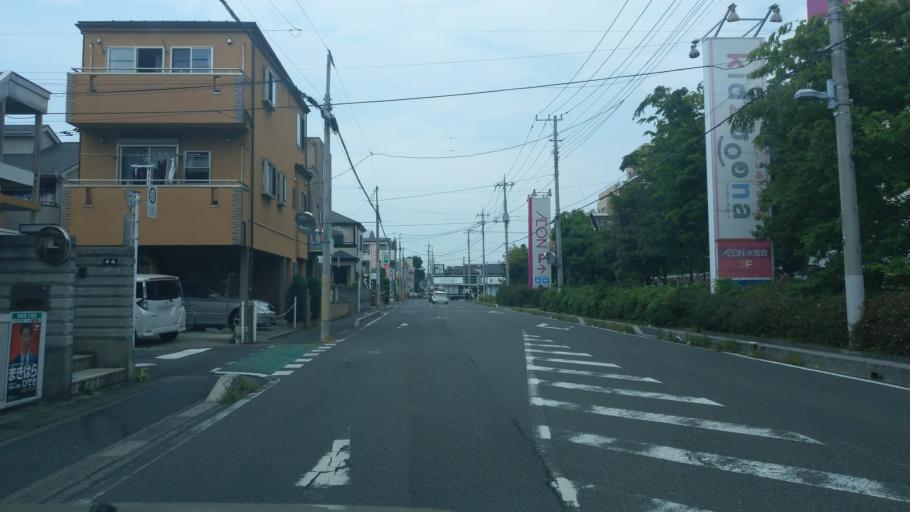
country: JP
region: Saitama
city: Yono
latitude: 35.9230
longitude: 139.6084
